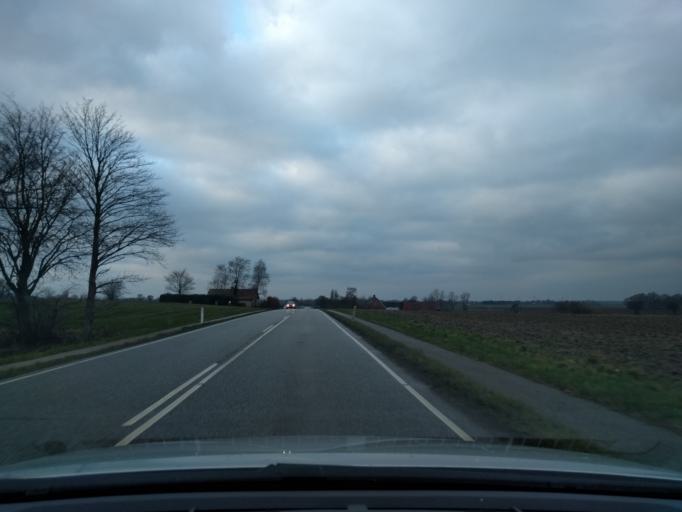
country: DK
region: Zealand
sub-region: Guldborgsund Kommune
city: Stubbekobing
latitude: 54.7973
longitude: 11.9862
